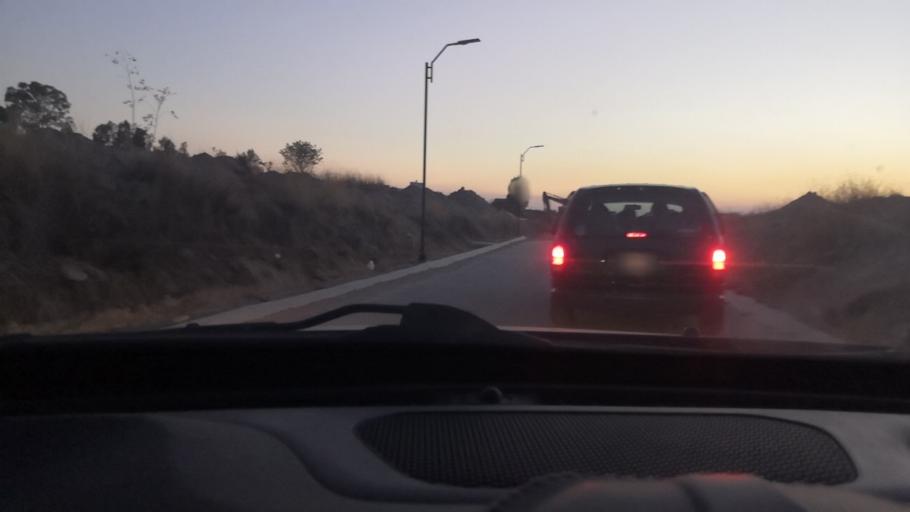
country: MX
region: Guanajuato
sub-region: Leon
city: Fraccionamiento Paseo de las Torres
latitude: 21.2272
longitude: -101.8063
